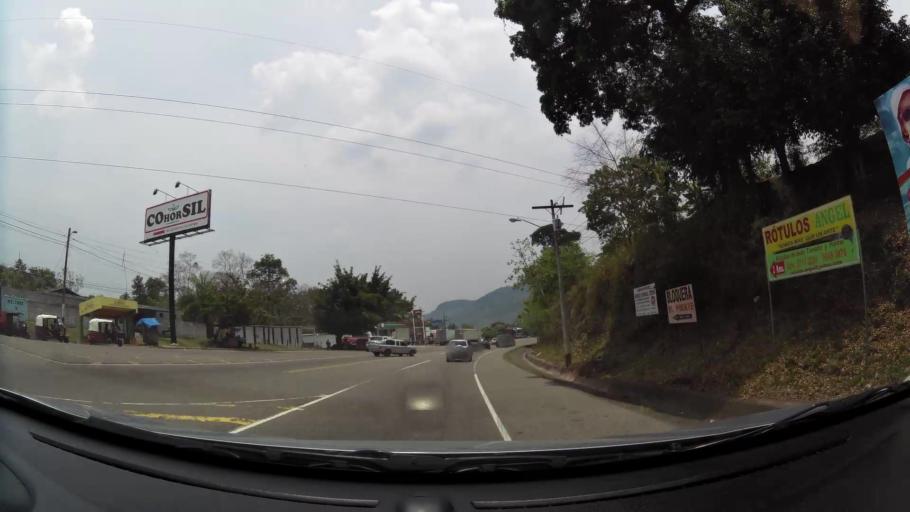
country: HN
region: Comayagua
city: Taulabe
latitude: 14.6954
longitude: -87.9611
